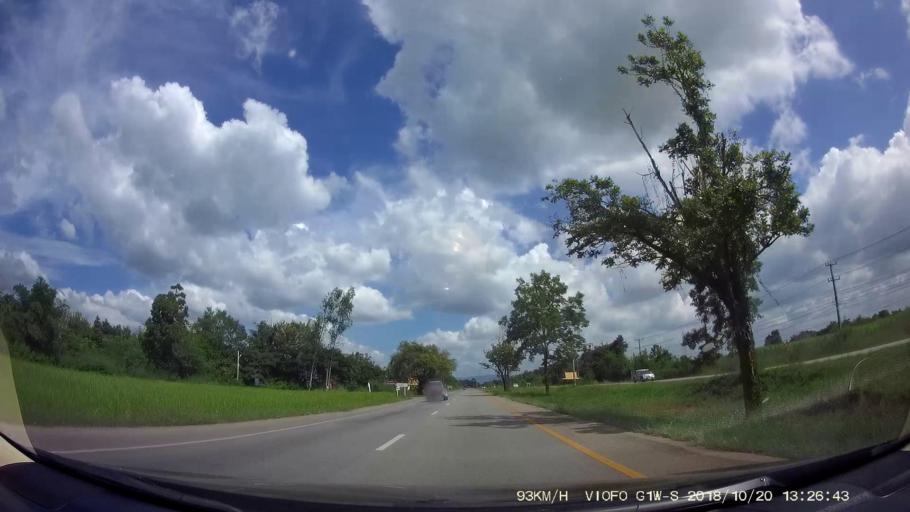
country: TH
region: Chaiyaphum
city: Khon San
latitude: 16.5934
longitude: 101.9503
